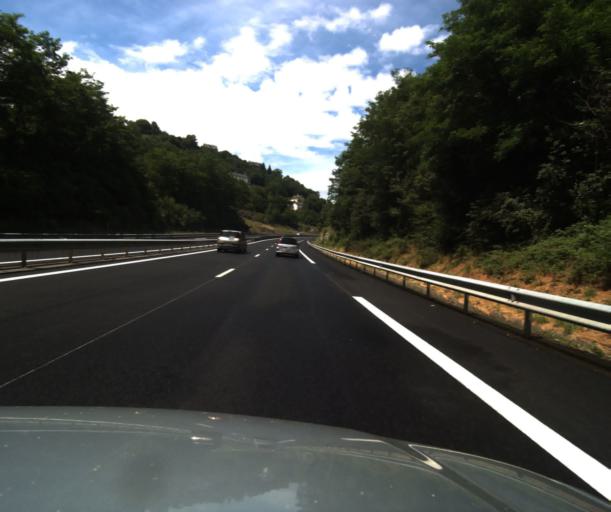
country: FR
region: Midi-Pyrenees
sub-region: Departement des Hautes-Pyrenees
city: Lourdes
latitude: 43.0686
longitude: -0.0425
